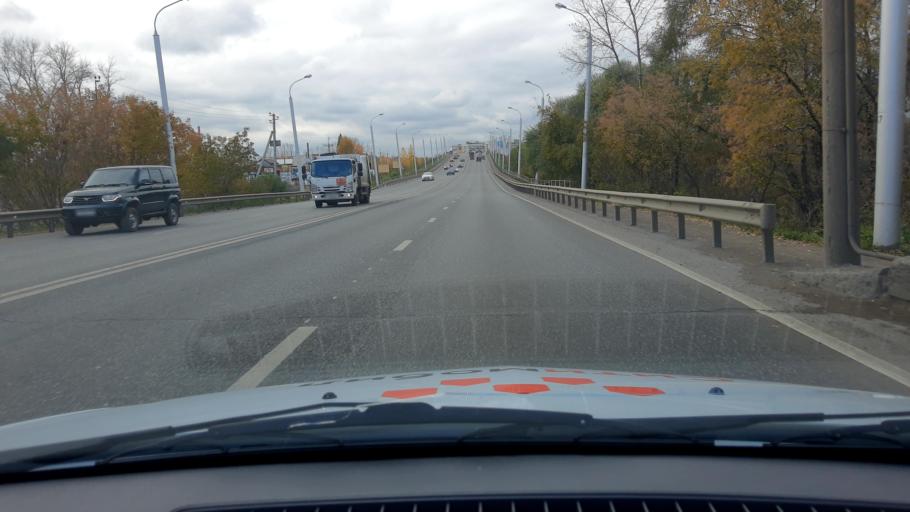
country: RU
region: Bashkortostan
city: Ufa
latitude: 54.8054
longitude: 56.1481
